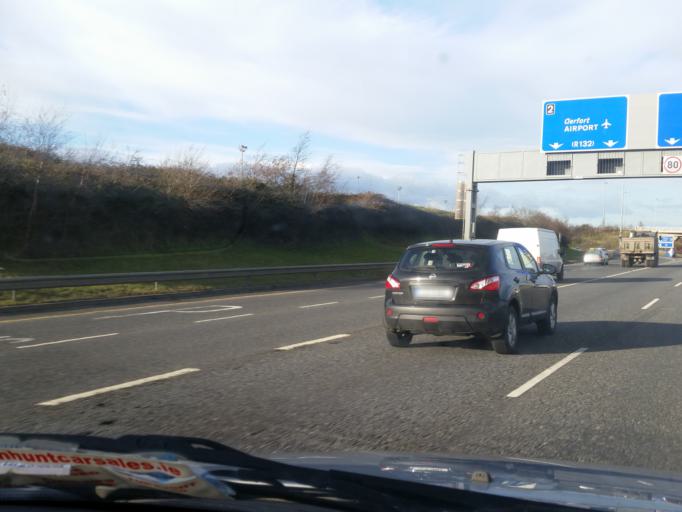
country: IE
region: Leinster
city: Kinsealy-Drinan
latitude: 53.4240
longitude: -6.2193
